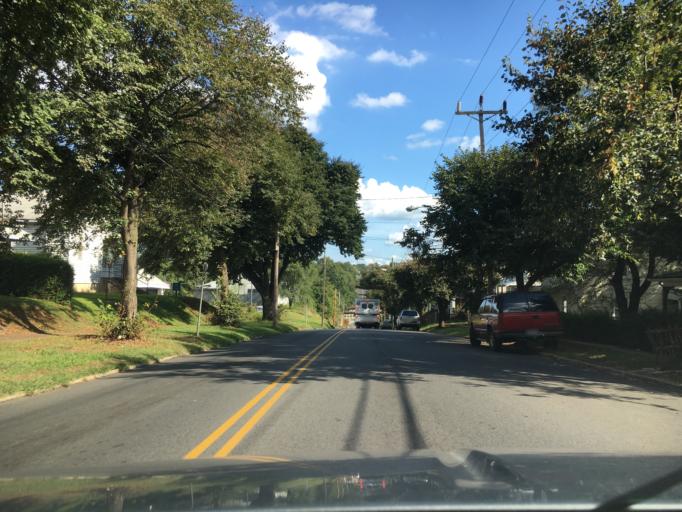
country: US
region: Virginia
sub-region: City of Lynchburg
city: Lynchburg
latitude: 37.3999
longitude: -79.1549
